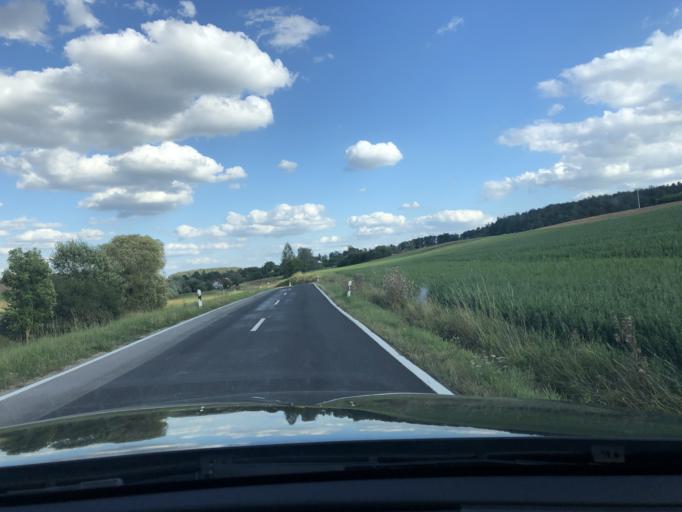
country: DE
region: Bavaria
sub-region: Regierungsbezirk Unterfranken
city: Kirchlauter
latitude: 50.0456
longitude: 10.7063
